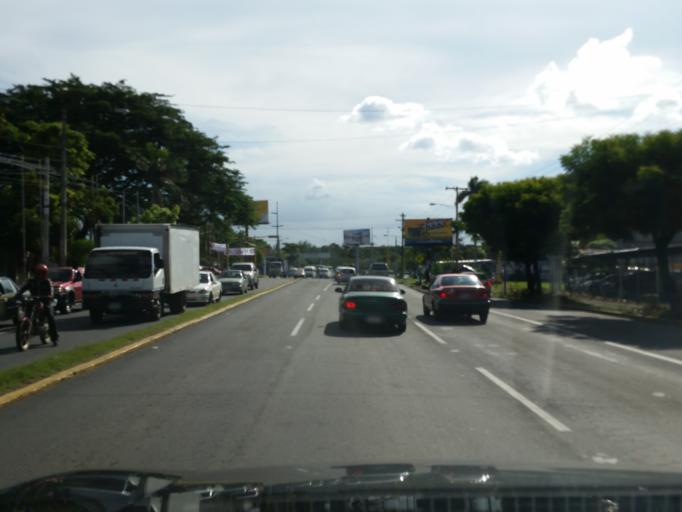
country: NI
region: Managua
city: Managua
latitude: 12.1253
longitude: -86.2739
